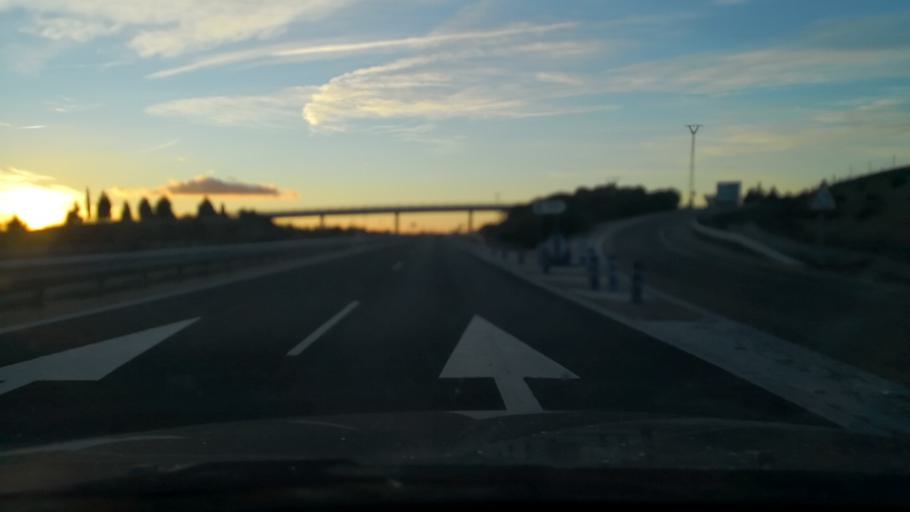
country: ES
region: Castille and Leon
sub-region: Provincia de Valladolid
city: Tordesillas
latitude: 41.5045
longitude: -5.0401
